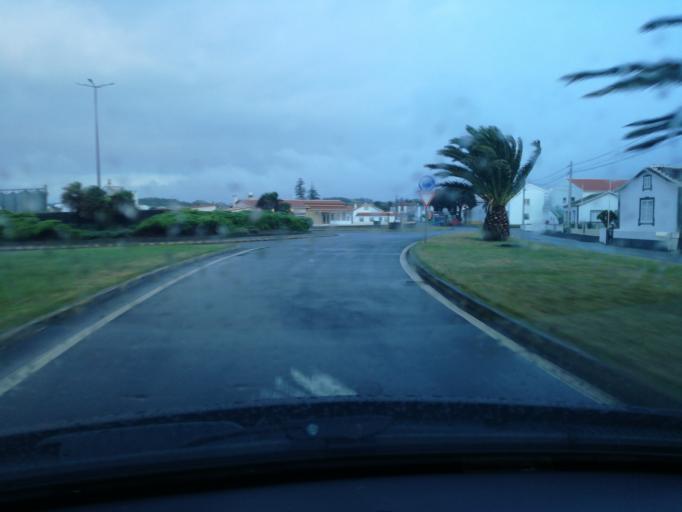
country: PT
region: Azores
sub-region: Praia da Vitoria
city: Praia da Vitoria
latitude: 38.7112
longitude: -27.0613
